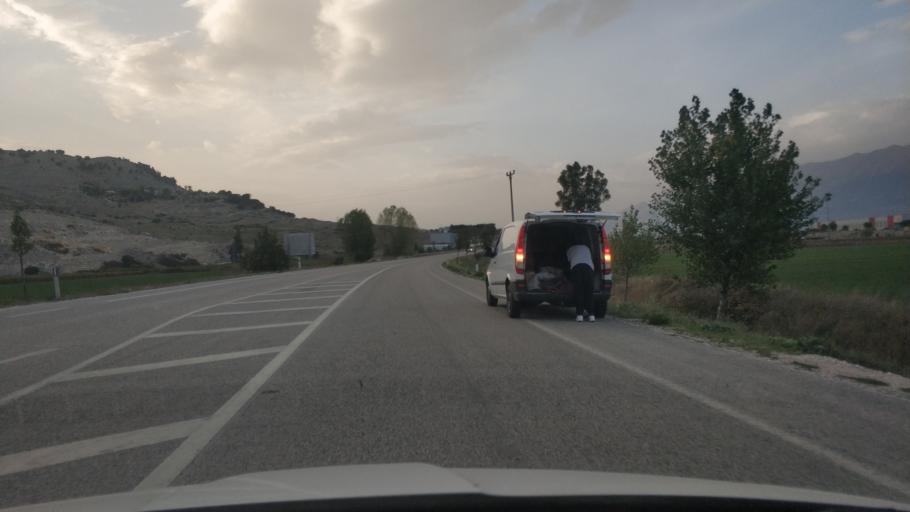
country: AL
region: Gjirokaster
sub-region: Rrethi i Gjirokastres
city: Libohove
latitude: 39.9689
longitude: 20.2379
